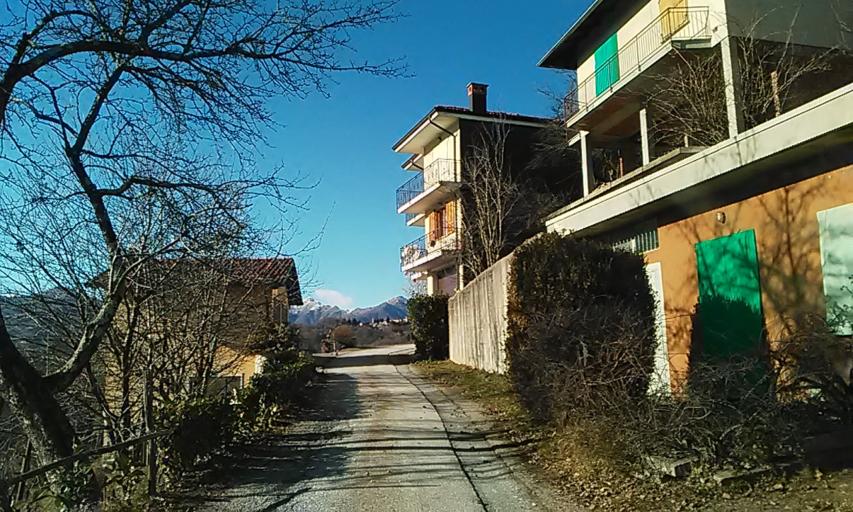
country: IT
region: Piedmont
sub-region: Provincia di Vercelli
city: Valduggia
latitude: 45.7334
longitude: 8.3114
